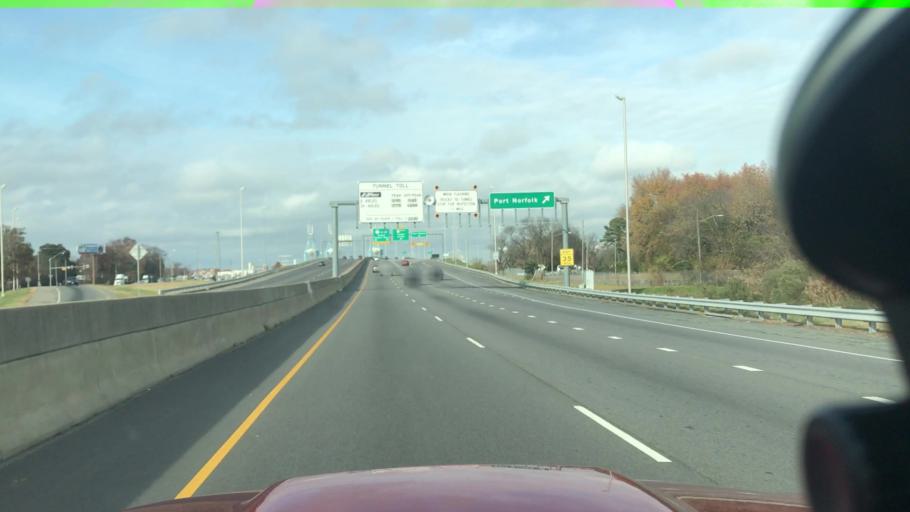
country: US
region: Virginia
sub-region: City of Portsmouth
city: Portsmouth
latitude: 36.8423
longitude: -76.3292
